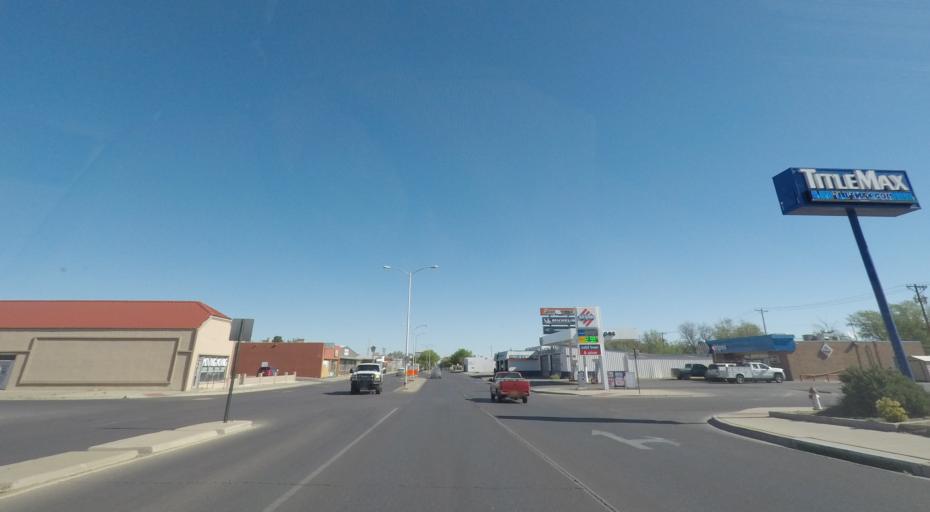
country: US
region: New Mexico
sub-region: Chaves County
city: Roswell
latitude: 33.3865
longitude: -104.5227
